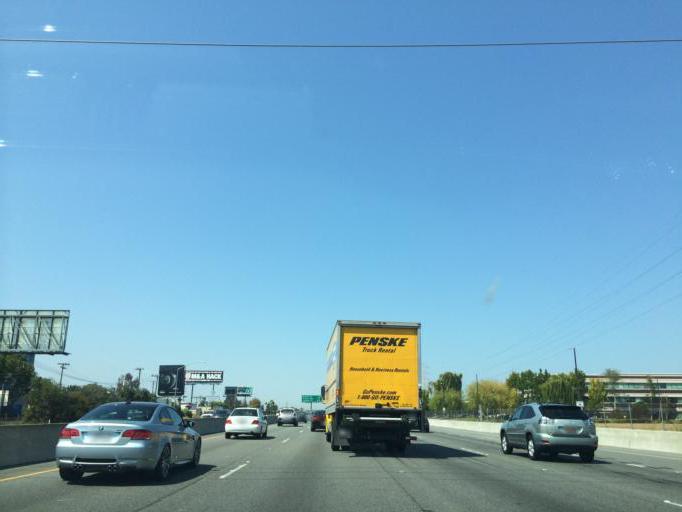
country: US
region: California
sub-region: San Mateo County
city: San Carlos
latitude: 37.5194
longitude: -122.2622
